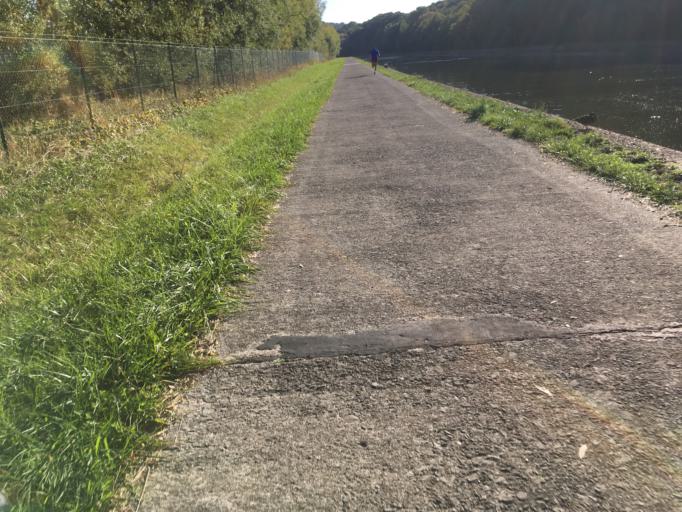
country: BE
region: Wallonia
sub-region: Province de Namur
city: Floreffe
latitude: 50.4465
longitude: 4.7616
